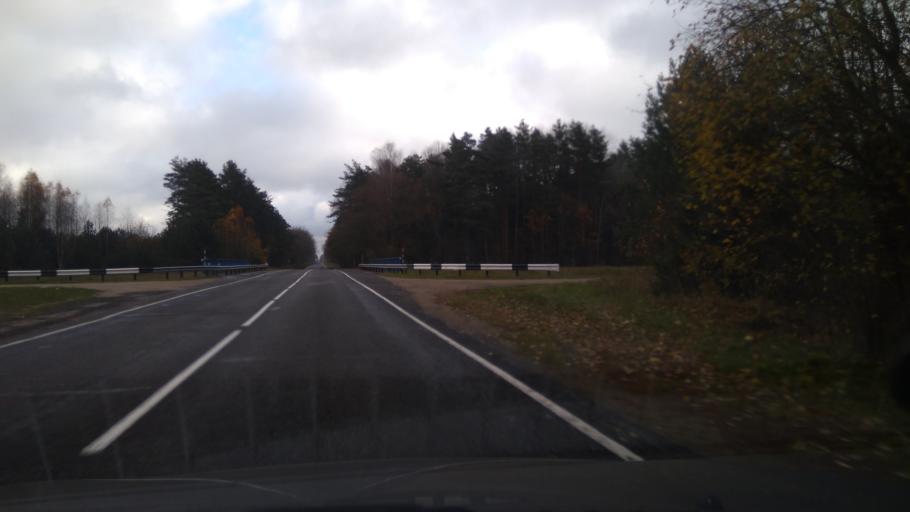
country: BY
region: Minsk
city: Slutsk
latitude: 53.2320
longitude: 27.6428
